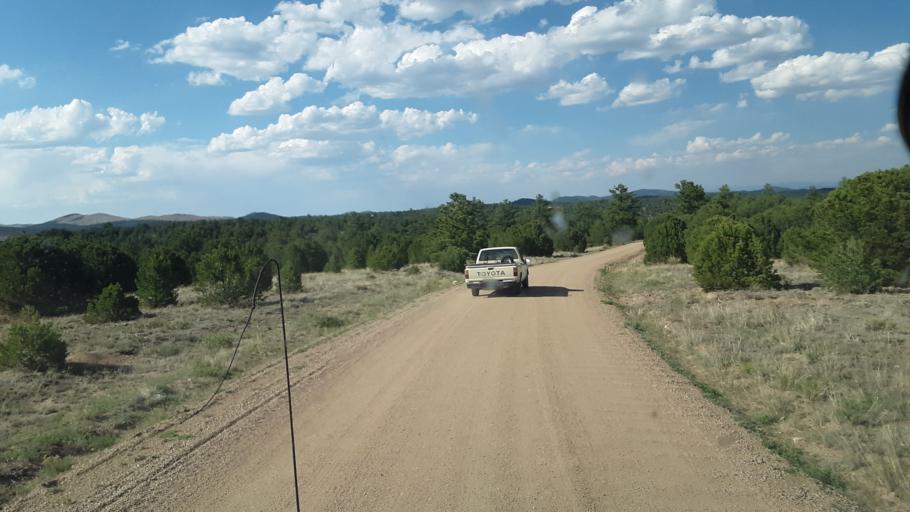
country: US
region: Colorado
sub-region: Custer County
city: Westcliffe
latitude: 38.2730
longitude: -105.4685
